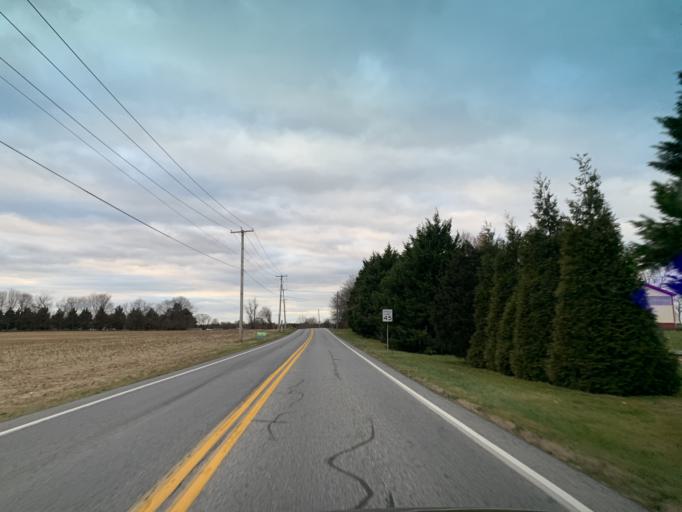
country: US
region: Pennsylvania
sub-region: York County
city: Shrewsbury
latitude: 39.7855
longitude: -76.6552
